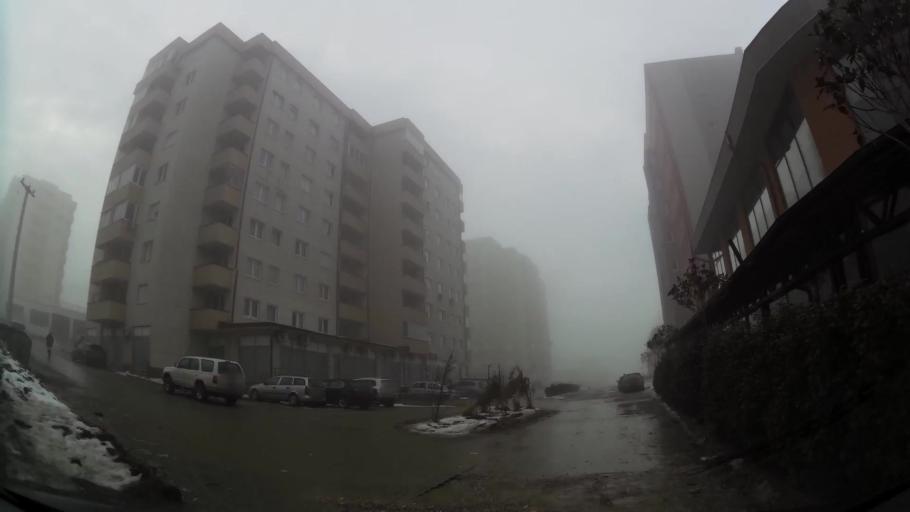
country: XK
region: Pristina
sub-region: Komuna e Prishtines
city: Pristina
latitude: 42.6402
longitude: 21.1529
